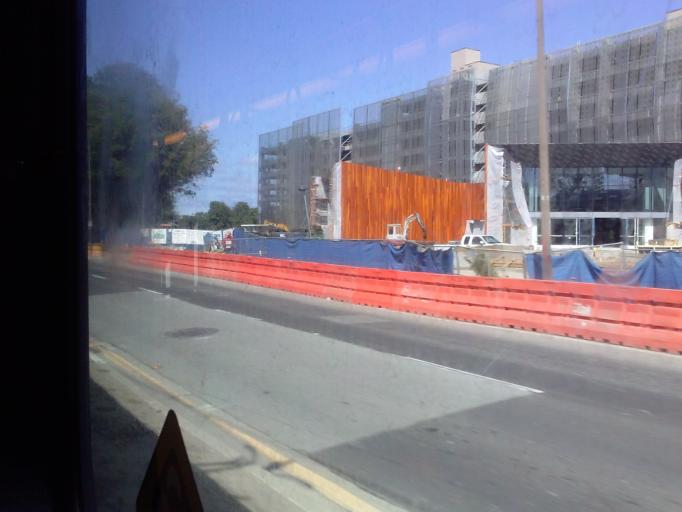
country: US
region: California
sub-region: Santa Clara County
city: Milpitas
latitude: 37.4089
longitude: -121.9466
